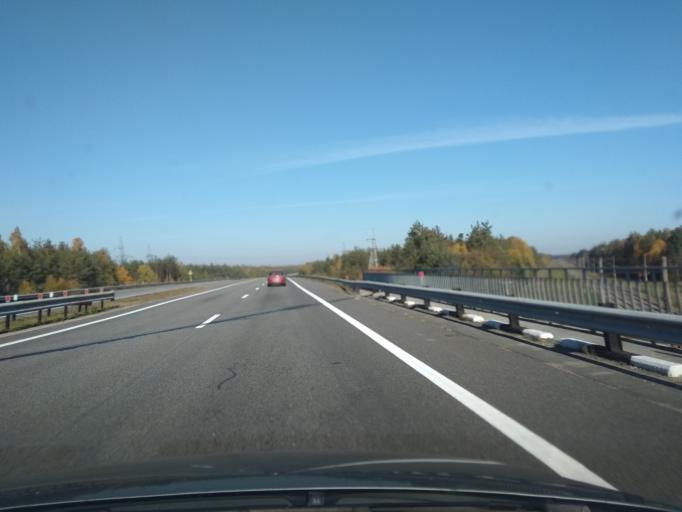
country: BY
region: Grodnenskaya
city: Zhyrovichy
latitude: 52.9130
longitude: 25.6826
